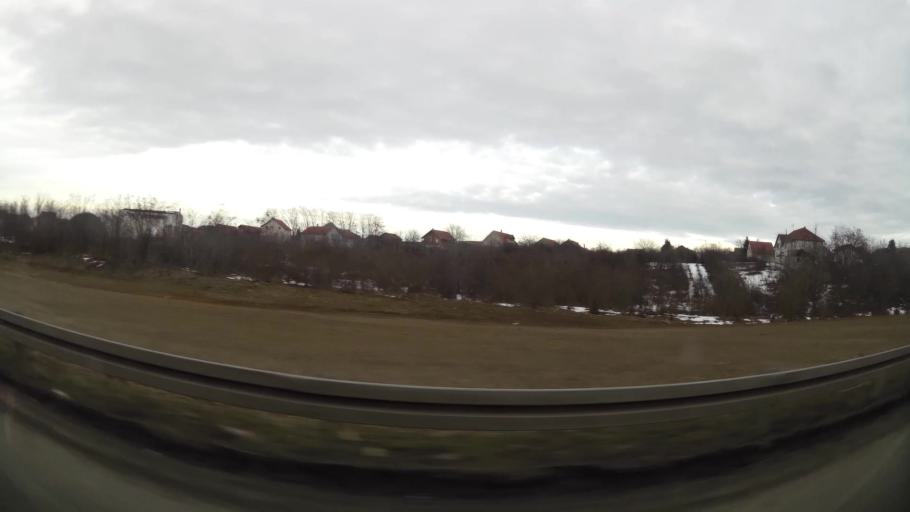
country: RS
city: Ostruznica
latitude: 44.7147
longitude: 20.3623
